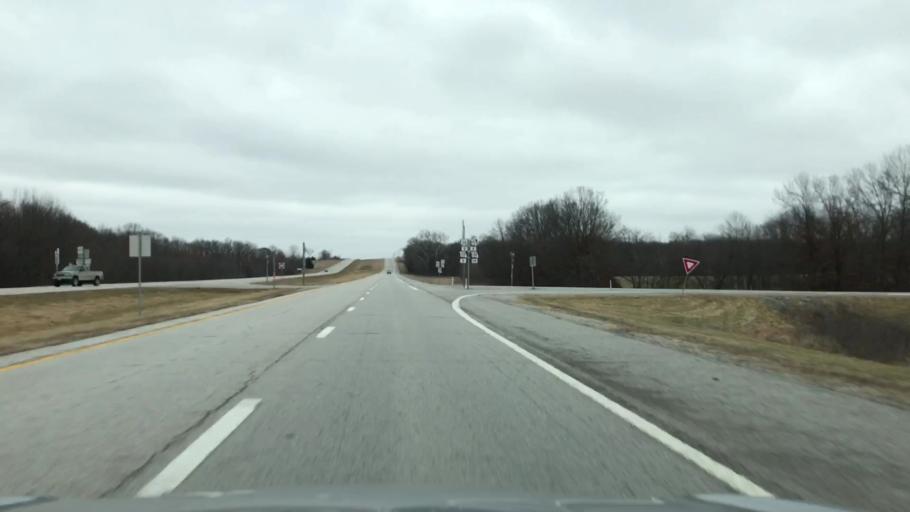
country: US
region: Missouri
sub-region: Linn County
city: Linneus
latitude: 39.7779
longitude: -93.2114
